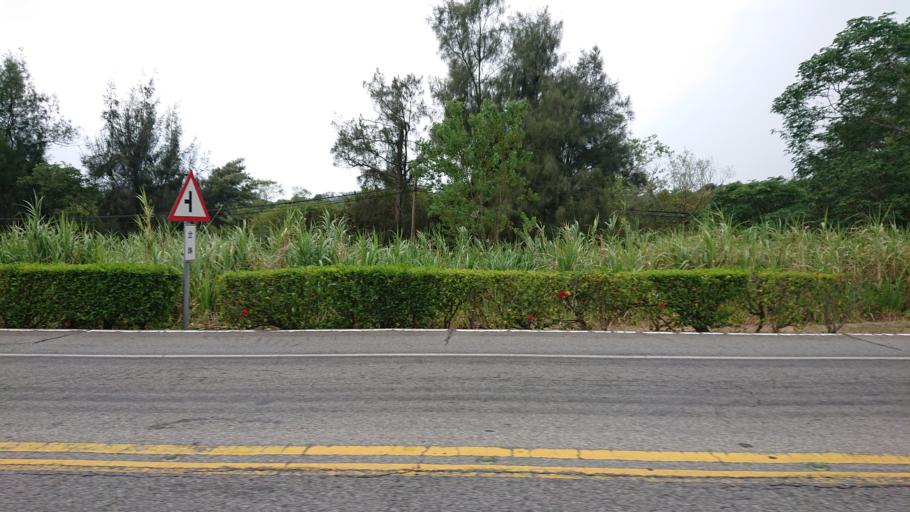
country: TW
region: Fukien
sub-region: Kinmen
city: Jincheng
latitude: 24.4454
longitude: 118.3871
